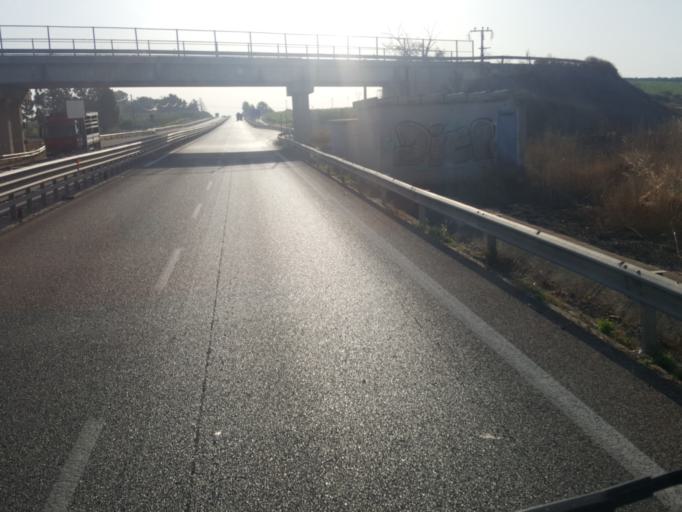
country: IT
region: Apulia
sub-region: Provincia di Foggia
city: Cerignola
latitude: 41.2746
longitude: 15.9699
